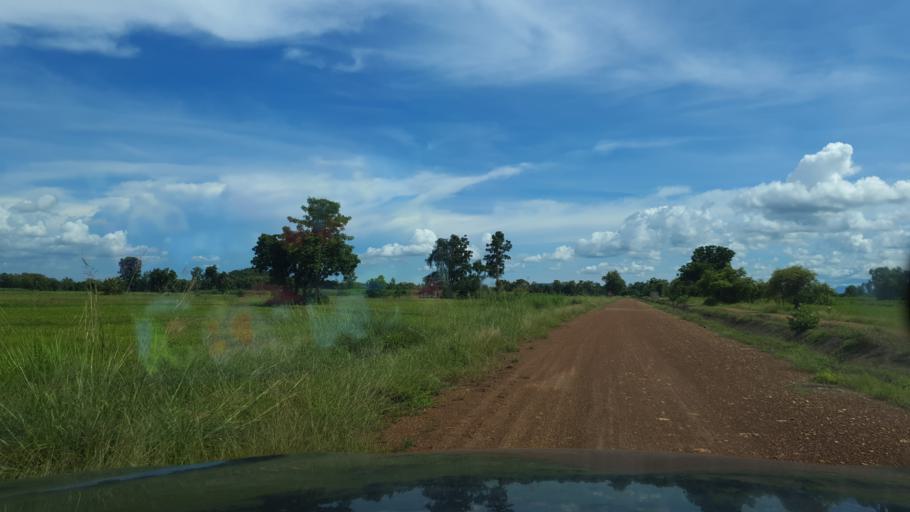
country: TH
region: Sukhothai
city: Thung Saliam
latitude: 17.3895
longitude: 99.6809
